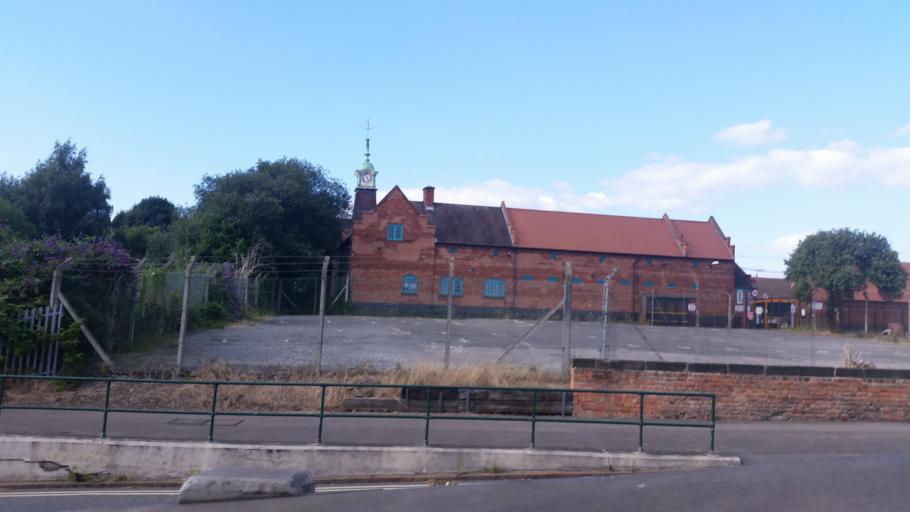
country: GB
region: England
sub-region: Derby
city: Derby
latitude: 52.9257
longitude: -1.4667
